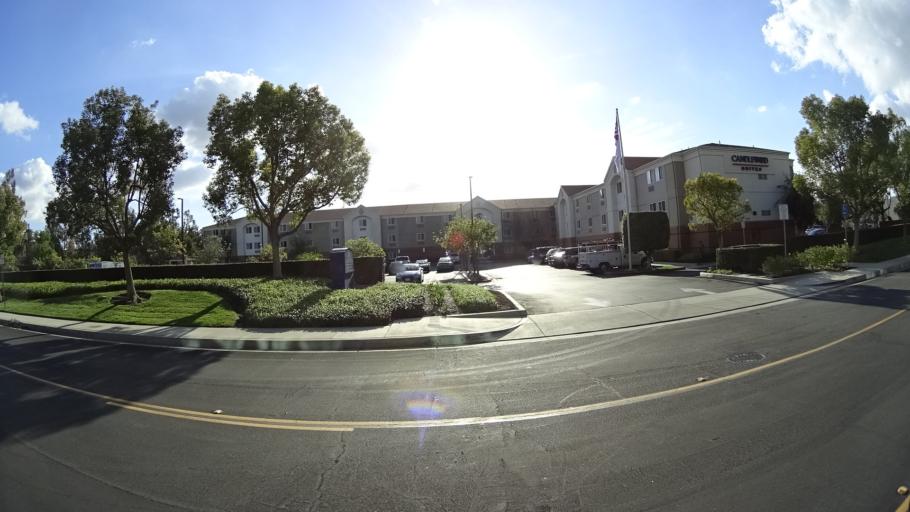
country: US
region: California
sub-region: Orange County
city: Lake Forest
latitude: 33.6591
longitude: -117.6980
